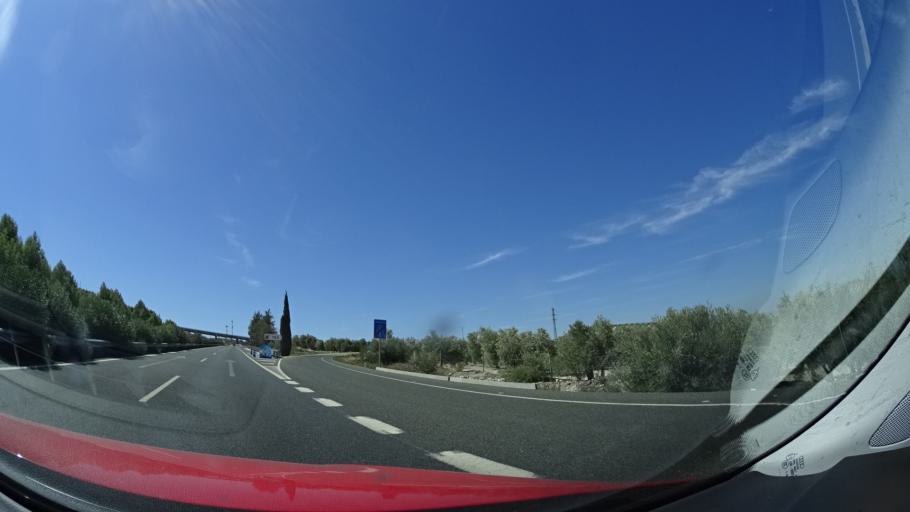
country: ES
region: Andalusia
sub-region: Provincia de Sevilla
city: Estepa
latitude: 37.2940
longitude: -4.8993
